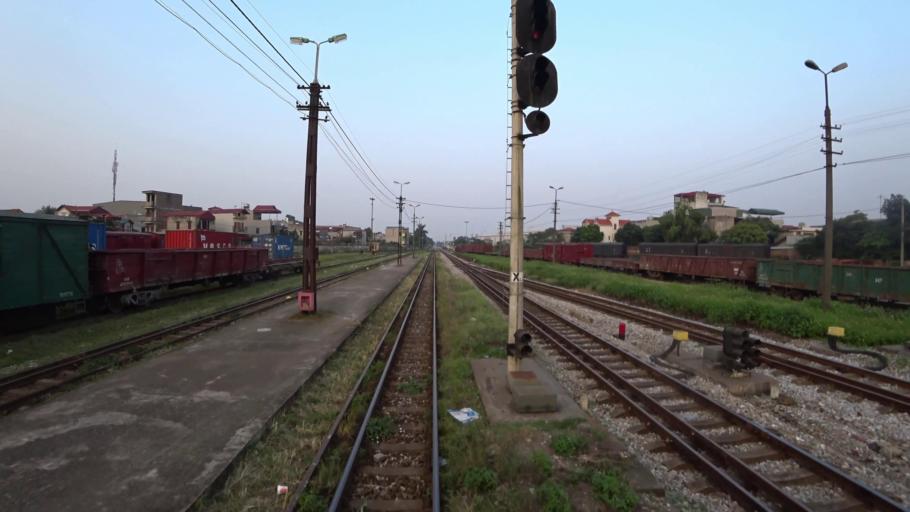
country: VN
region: Ha Noi
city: Dong Anh
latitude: 21.1035
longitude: 105.9033
